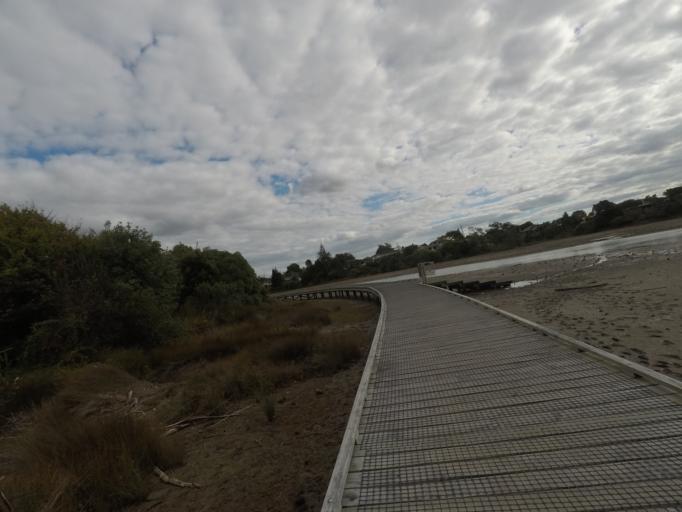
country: NZ
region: Auckland
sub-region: Auckland
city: Papakura
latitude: -37.0629
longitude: 174.9333
